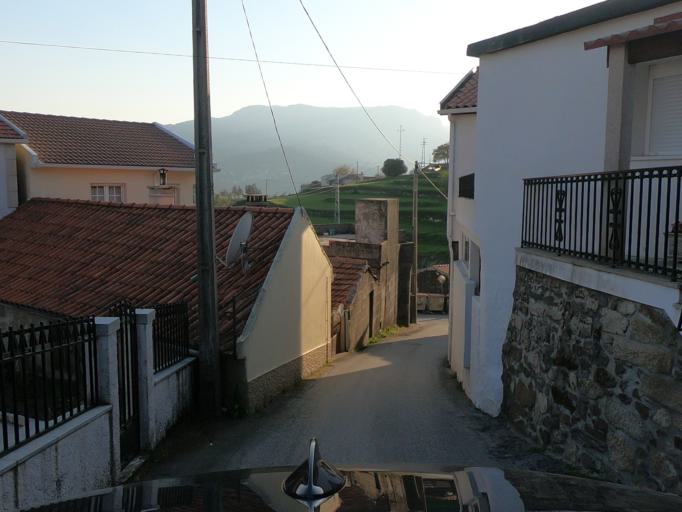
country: PT
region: Vila Real
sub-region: Santa Marta de Penaguiao
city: Santa Marta de Penaguiao
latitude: 41.2603
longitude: -7.8098
